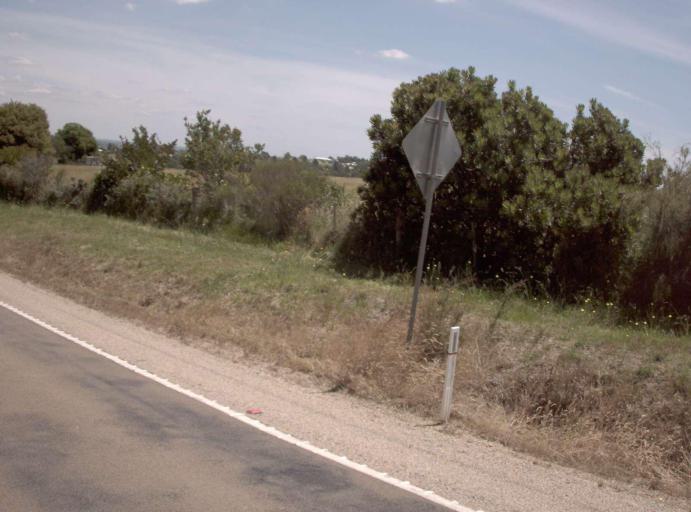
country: AU
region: Victoria
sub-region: East Gippsland
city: Bairnsdale
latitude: -37.8007
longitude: 147.6577
